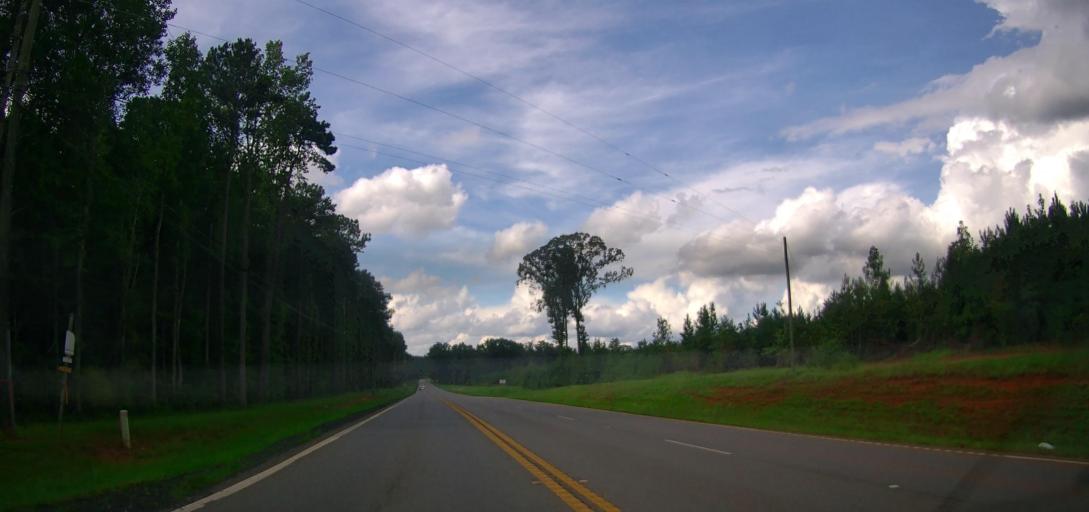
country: US
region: Georgia
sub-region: Harris County
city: Hamilton
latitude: 32.7239
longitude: -84.8741
